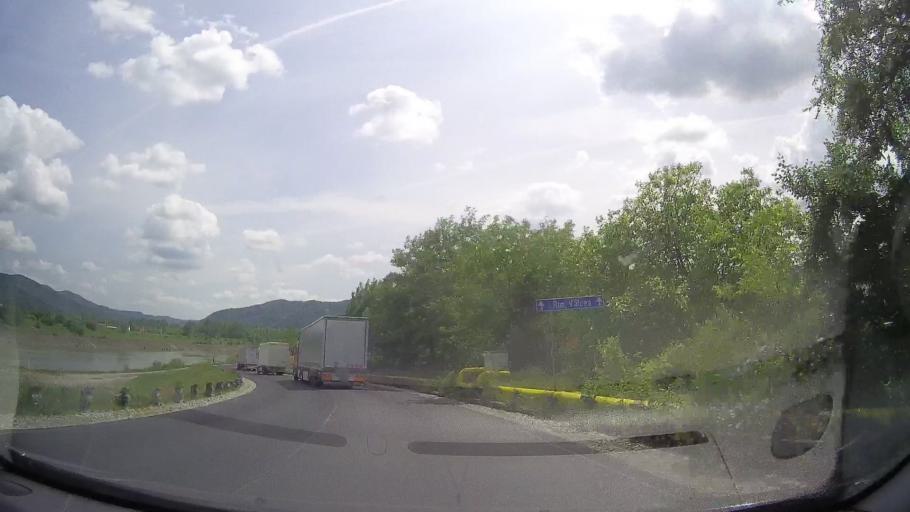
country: RO
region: Valcea
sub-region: Oras Calimanesti
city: Jiblea Veche
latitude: 45.2397
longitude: 24.3445
